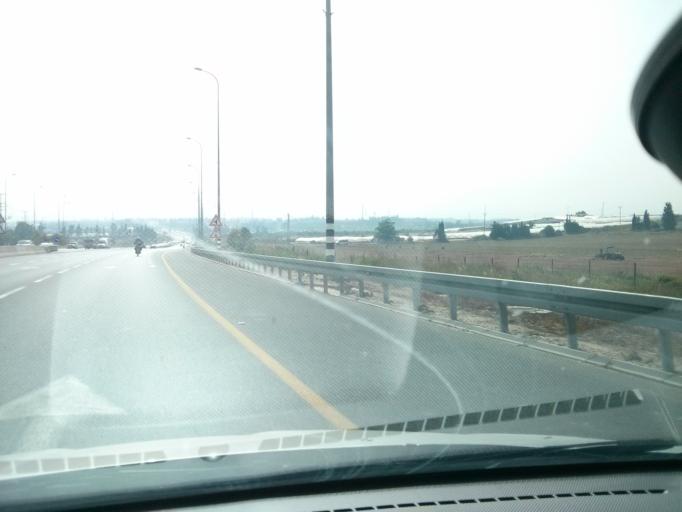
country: IL
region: Central District
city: Even Yehuda
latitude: 32.2554
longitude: 34.8768
